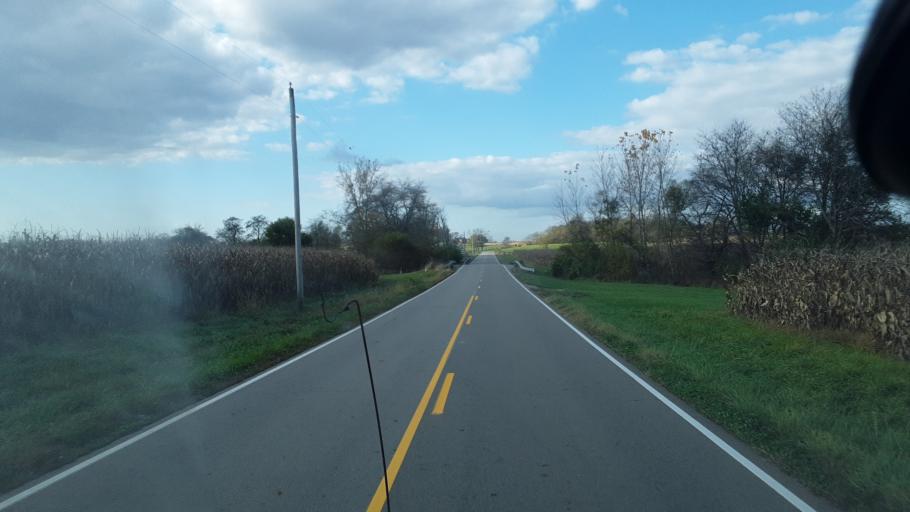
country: US
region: Ohio
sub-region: Highland County
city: Greenfield
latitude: 39.4202
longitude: -83.4469
